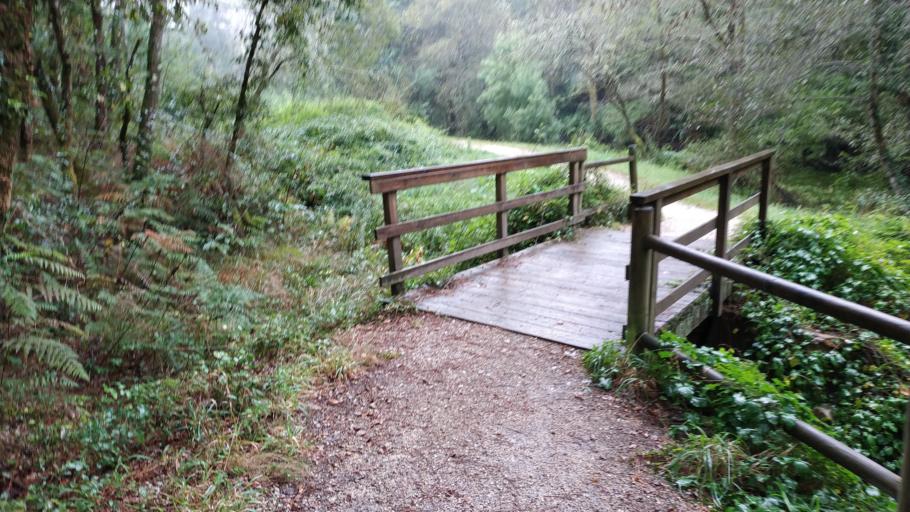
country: ES
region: Galicia
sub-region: Provincia da Coruna
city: Negreira
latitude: 42.9083
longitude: -8.7448
